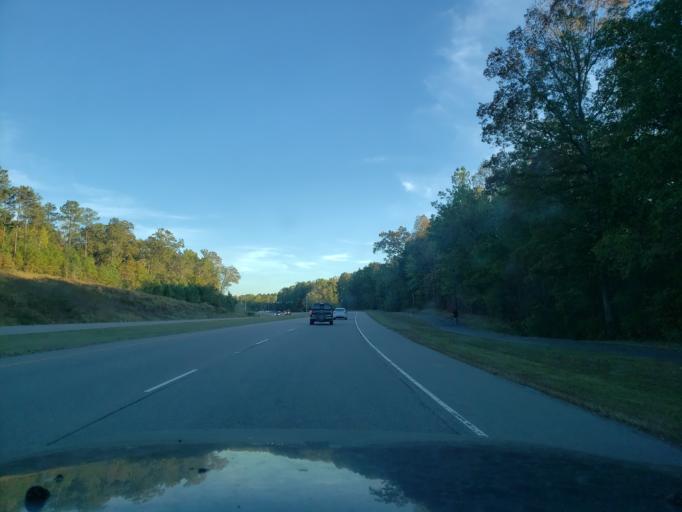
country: US
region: North Carolina
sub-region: Wake County
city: Morrisville
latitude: 35.8489
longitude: -78.8590
